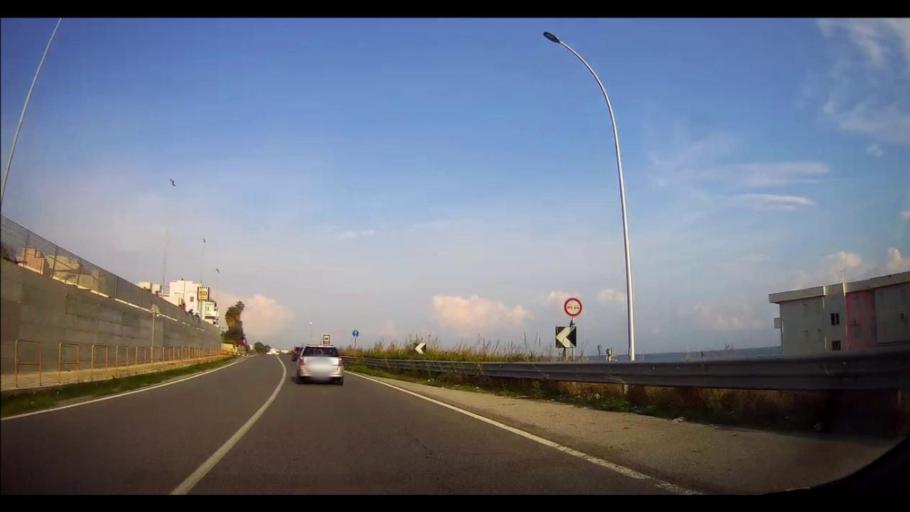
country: IT
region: Calabria
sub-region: Provincia di Cosenza
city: Cariati
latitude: 39.5073
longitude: 16.9356
